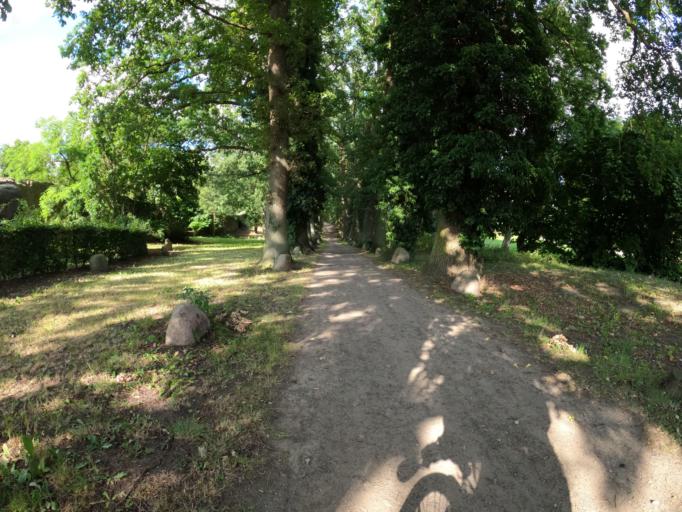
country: DE
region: Mecklenburg-Vorpommern
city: Woldegk
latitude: 53.4579
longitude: 13.5851
